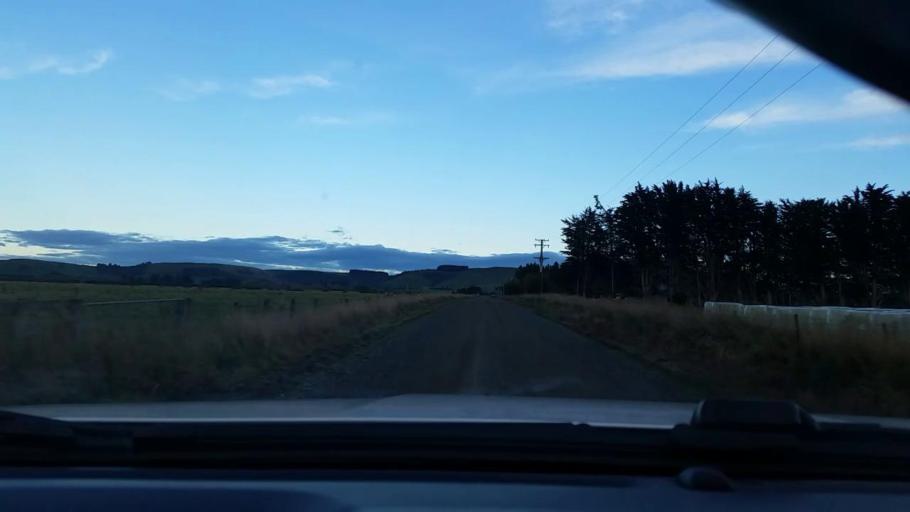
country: NZ
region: Southland
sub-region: Southland District
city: Winton
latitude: -46.1080
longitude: 168.4437
